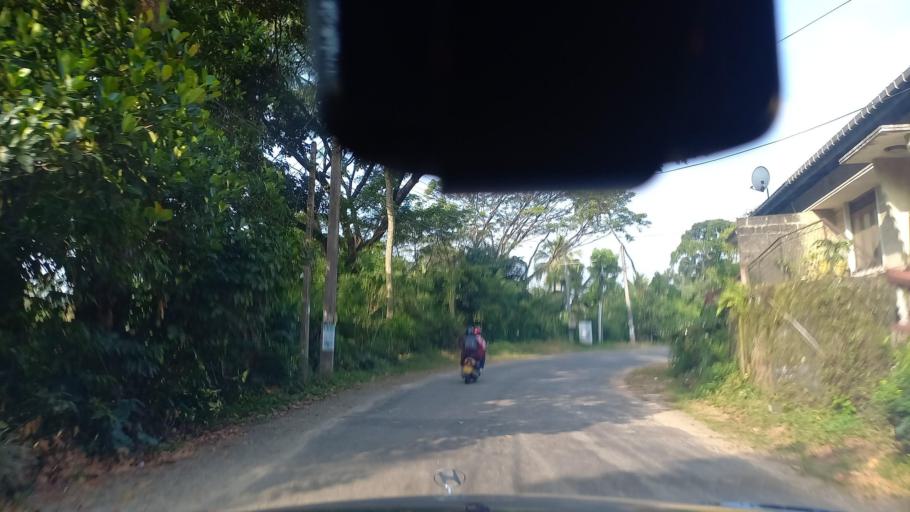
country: LK
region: Central
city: Gampola
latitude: 7.2196
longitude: 80.6078
